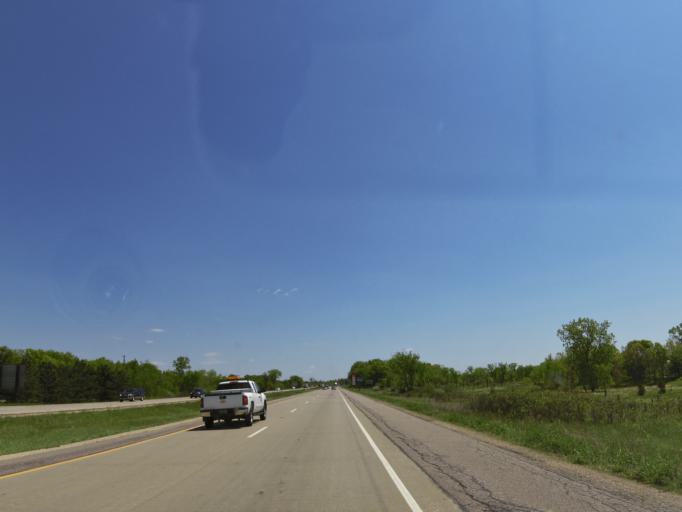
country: US
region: Wisconsin
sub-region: Juneau County
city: New Lisbon
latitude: 43.8795
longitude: -90.1408
